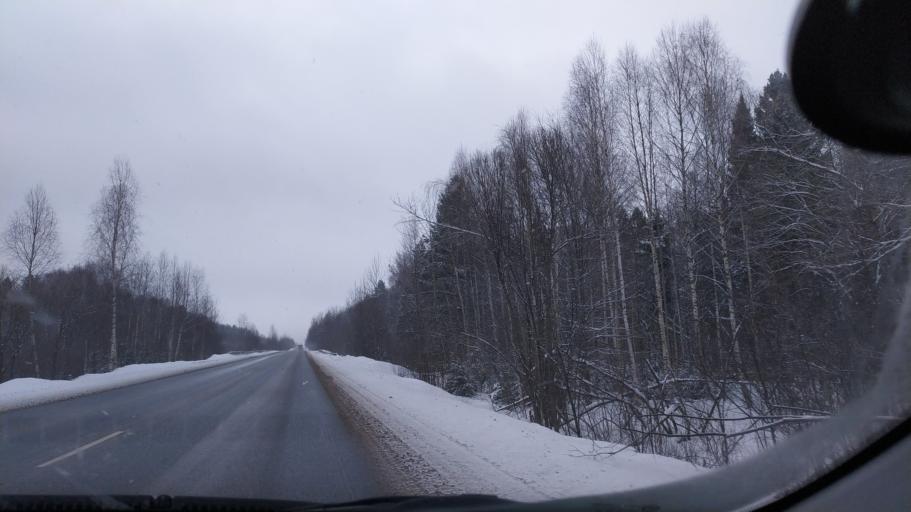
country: RU
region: Mariy-El
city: Krasnogorskiy
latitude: 56.1651
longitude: 48.2028
